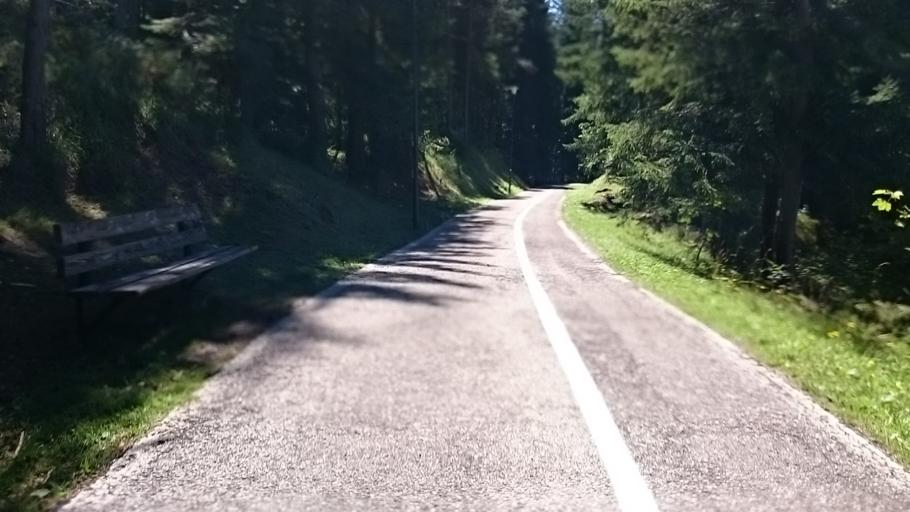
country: IT
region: Veneto
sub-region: Provincia di Belluno
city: San Vito
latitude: 46.4707
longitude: 12.2062
